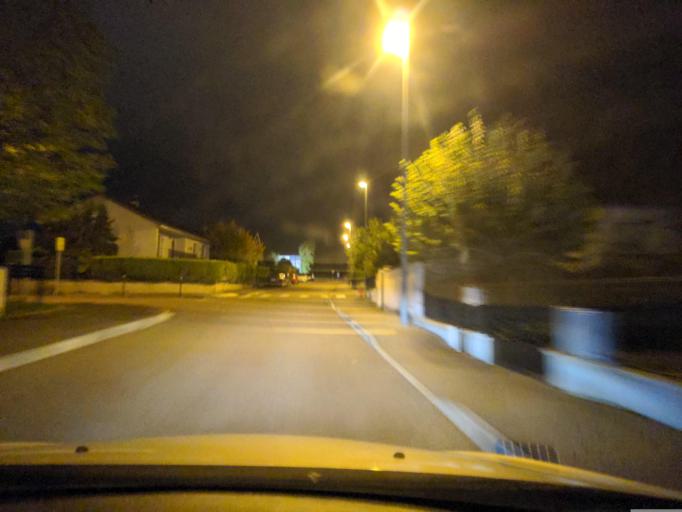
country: FR
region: Bourgogne
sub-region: Departement de la Cote-d'Or
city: Saint-Apollinaire
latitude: 47.3306
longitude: 5.0883
